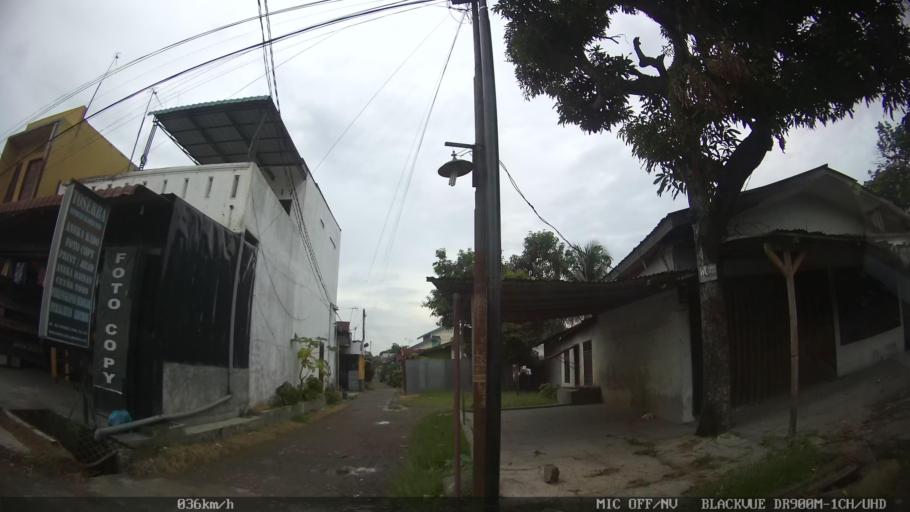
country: ID
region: North Sumatra
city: Sunggal
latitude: 3.6208
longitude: 98.5962
